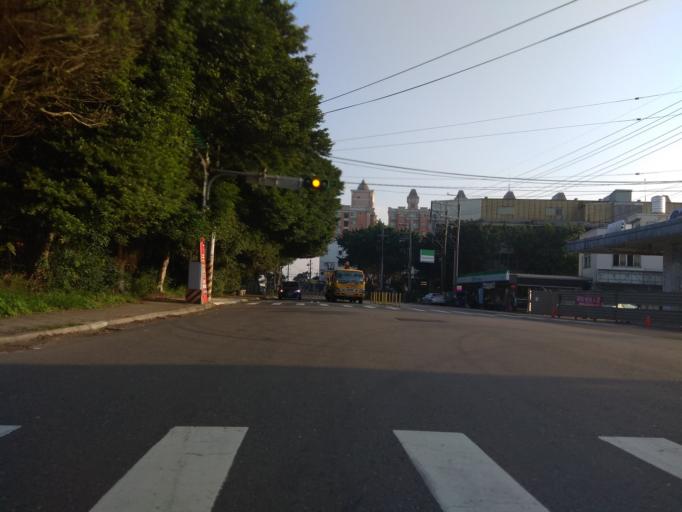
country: TW
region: Taiwan
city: Daxi
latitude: 24.9241
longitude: 121.1769
